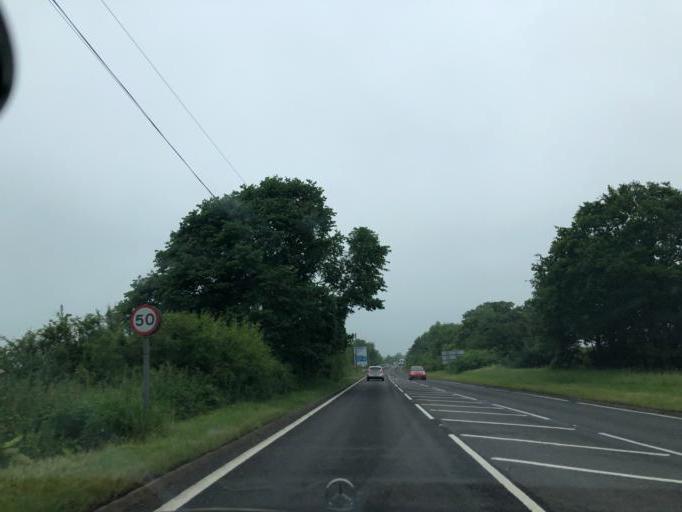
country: GB
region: England
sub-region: Warwickshire
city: Warwick
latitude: 52.2377
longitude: -1.5529
